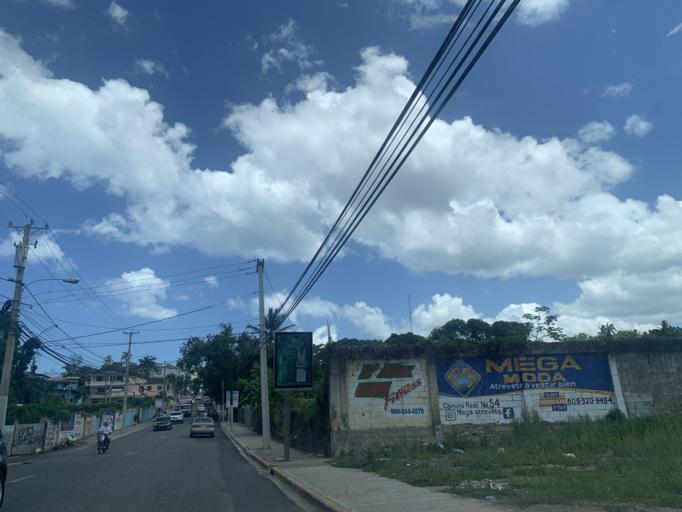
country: DO
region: Puerto Plata
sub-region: Puerto Plata
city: Puerto Plata
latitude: 19.7914
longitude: -70.6957
